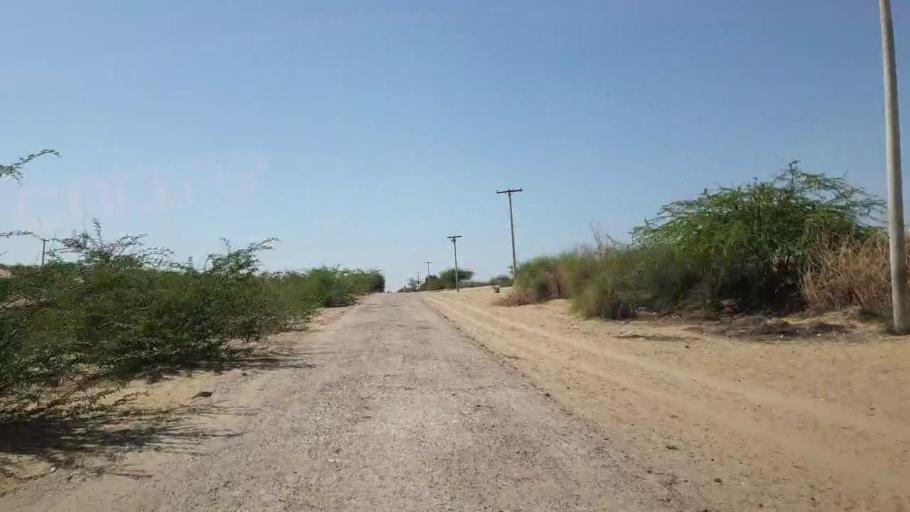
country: PK
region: Sindh
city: Umarkot
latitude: 25.1682
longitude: 69.9673
